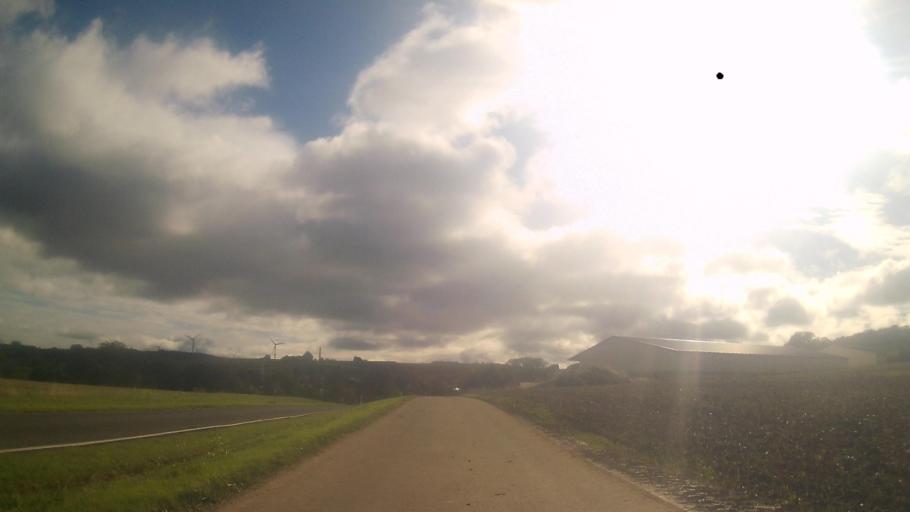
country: DE
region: Rheinland-Pfalz
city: Sulzheim
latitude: 49.8243
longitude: 8.0838
